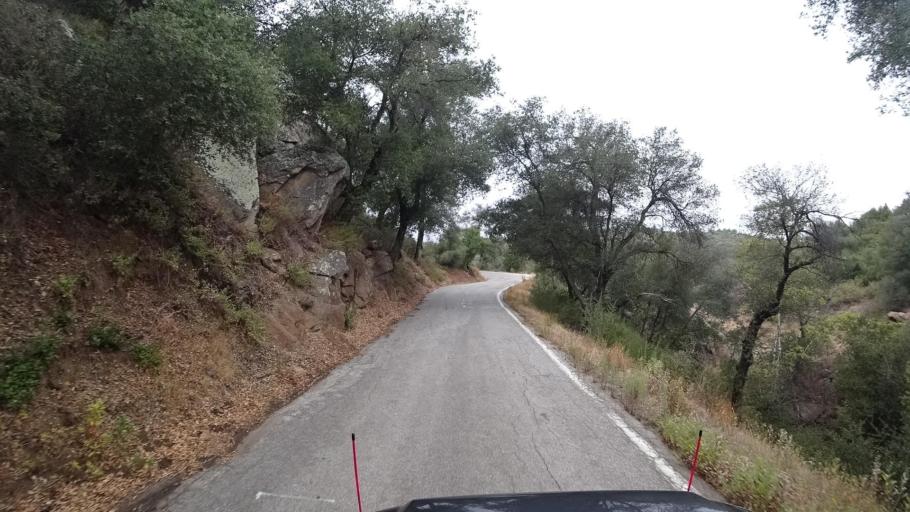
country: US
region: California
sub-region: San Diego County
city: Julian
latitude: 33.0299
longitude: -116.6365
